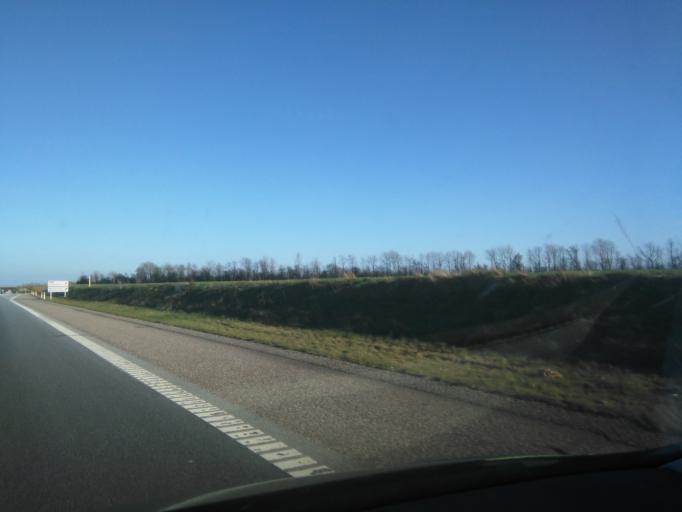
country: DK
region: Central Jutland
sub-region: Herning Kommune
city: Snejbjerg
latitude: 56.1214
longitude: 8.8991
